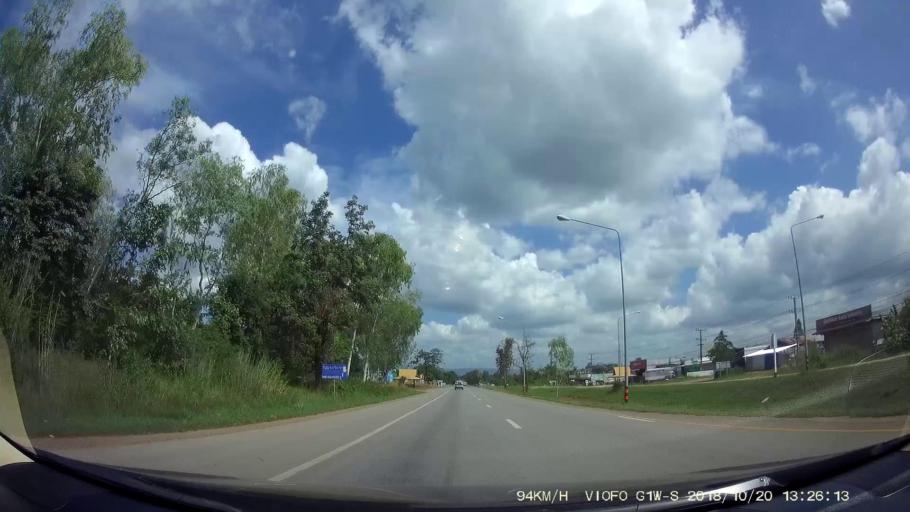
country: TH
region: Chaiyaphum
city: Khon San
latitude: 16.5940
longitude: 101.9431
